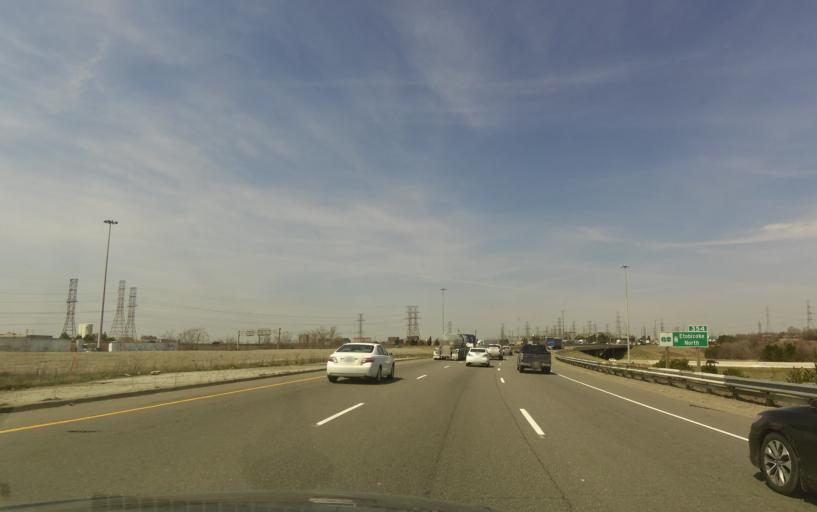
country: CA
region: Ontario
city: Etobicoke
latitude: 43.6742
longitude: -79.5775
